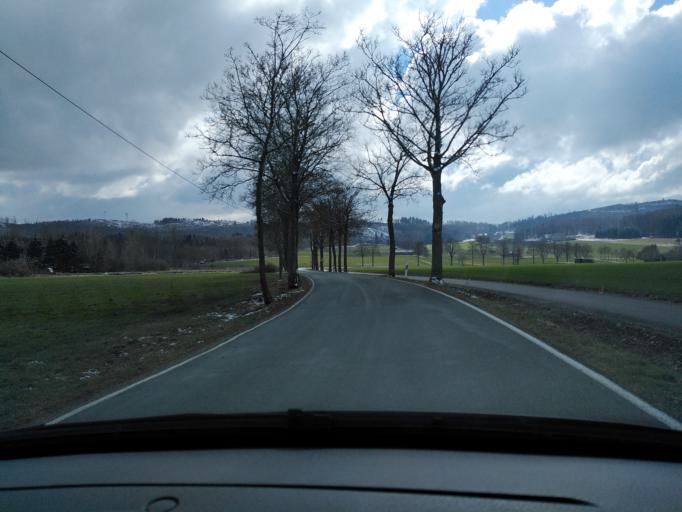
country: DE
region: North Rhine-Westphalia
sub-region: Regierungsbezirk Arnsberg
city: Brilon
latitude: 51.4013
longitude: 8.6330
